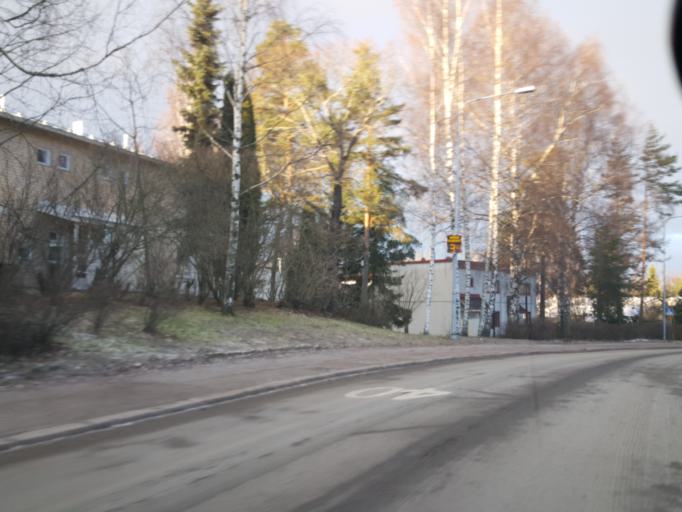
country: FI
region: Uusimaa
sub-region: Helsinki
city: Vantaa
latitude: 60.2498
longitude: 24.9878
